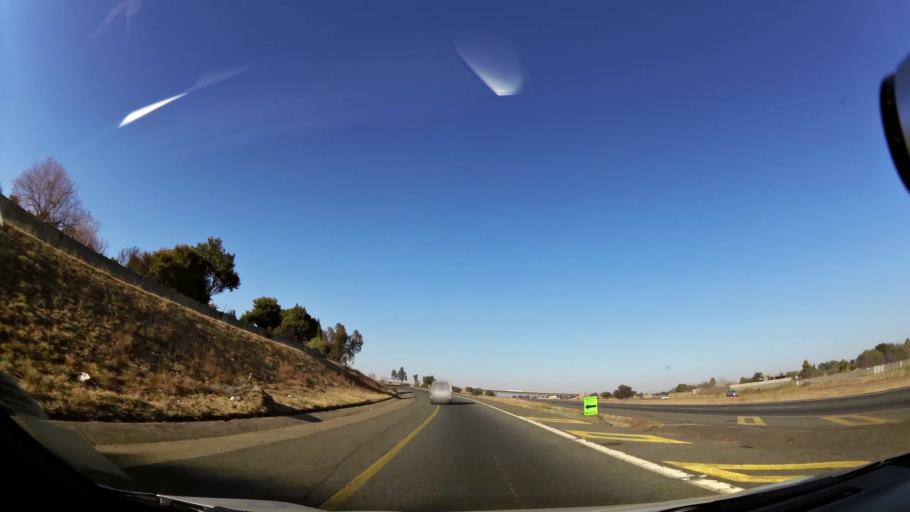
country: ZA
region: Gauteng
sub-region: Ekurhuleni Metropolitan Municipality
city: Germiston
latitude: -26.3474
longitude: 28.1025
